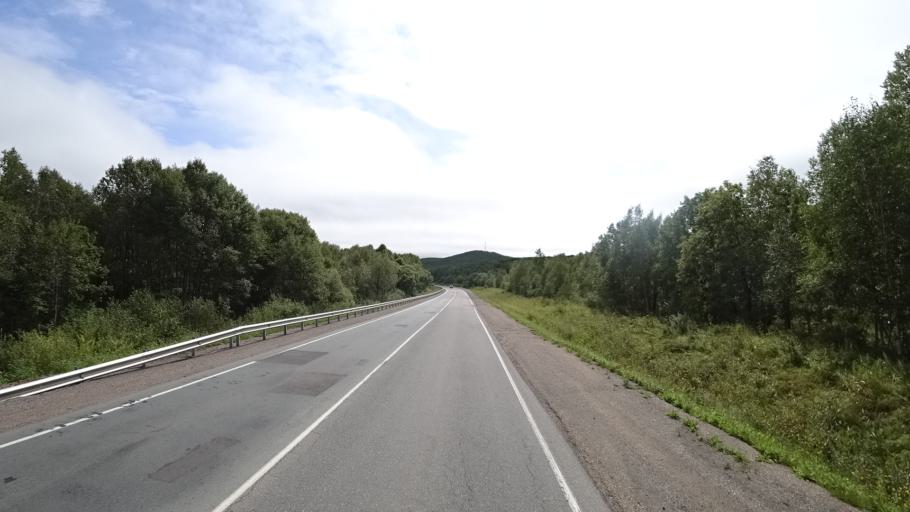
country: RU
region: Primorskiy
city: Lyalichi
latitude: 44.1187
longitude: 132.4195
